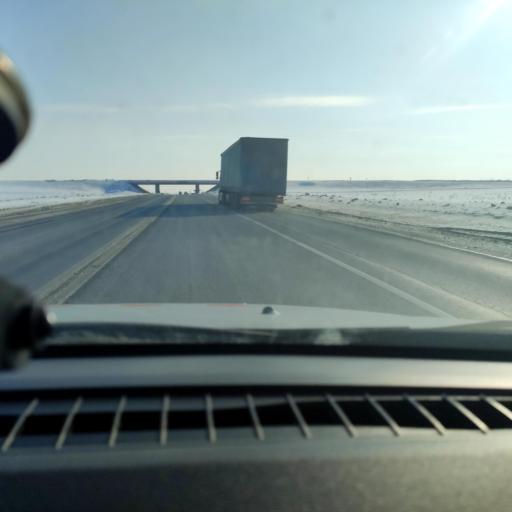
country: RU
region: Samara
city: Petra-Dubrava
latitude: 53.3424
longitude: 50.4513
